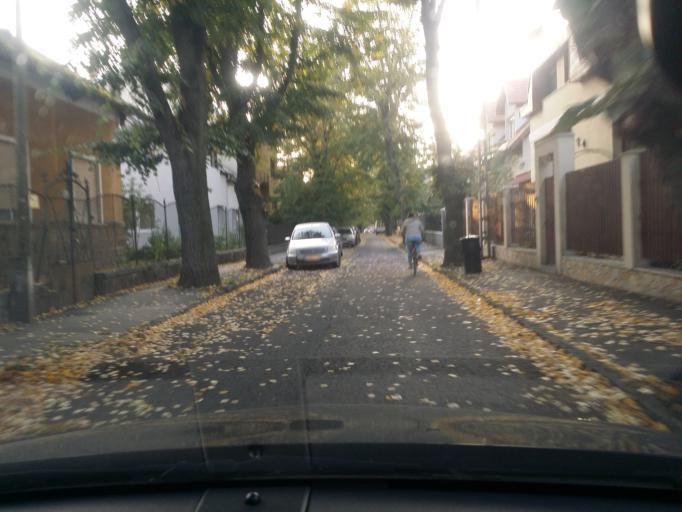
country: HU
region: Budapest
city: Budapest XV. keruelet
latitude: 47.5661
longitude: 19.1061
